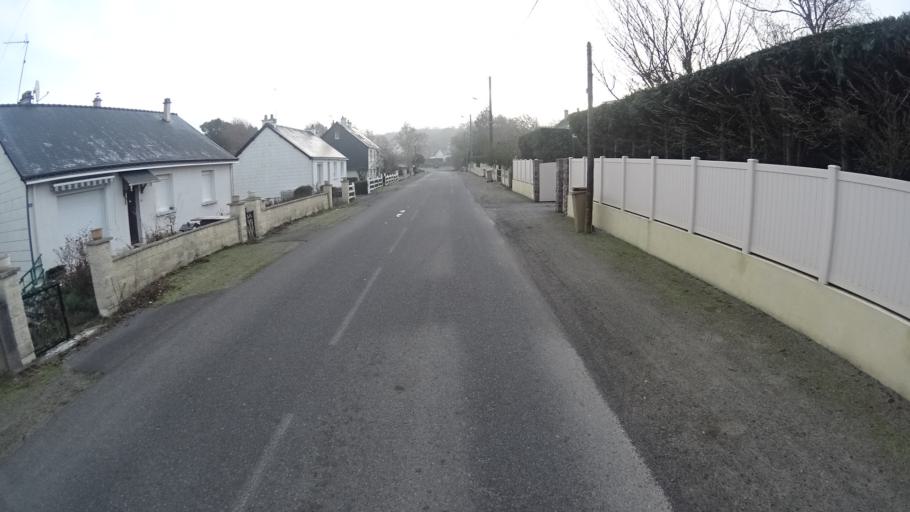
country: FR
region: Pays de la Loire
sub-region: Departement de la Loire-Atlantique
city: Saint-Nicolas-de-Redon
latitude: 47.6487
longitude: -2.0550
